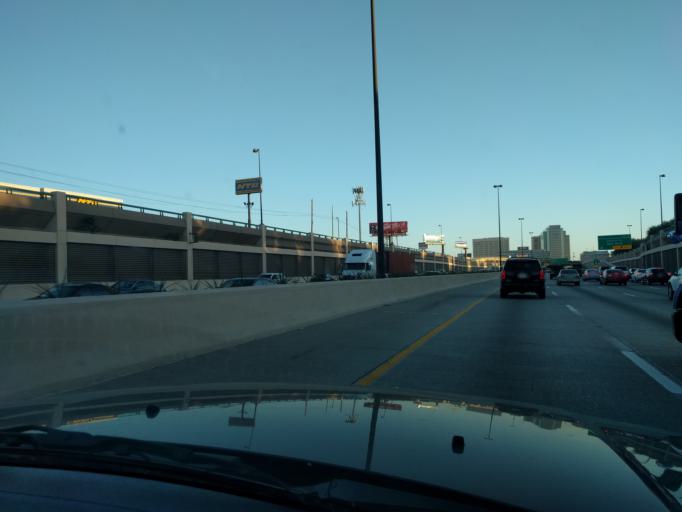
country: US
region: Texas
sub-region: Dallas County
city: University Park
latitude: 32.8562
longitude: -96.7704
